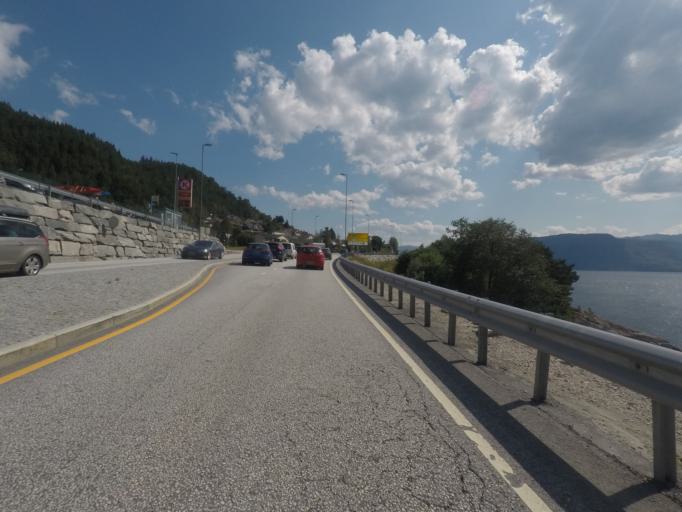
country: NO
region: Sogn og Fjordane
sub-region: Hyllestad
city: Hyllestad
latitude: 61.1032
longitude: 5.5115
